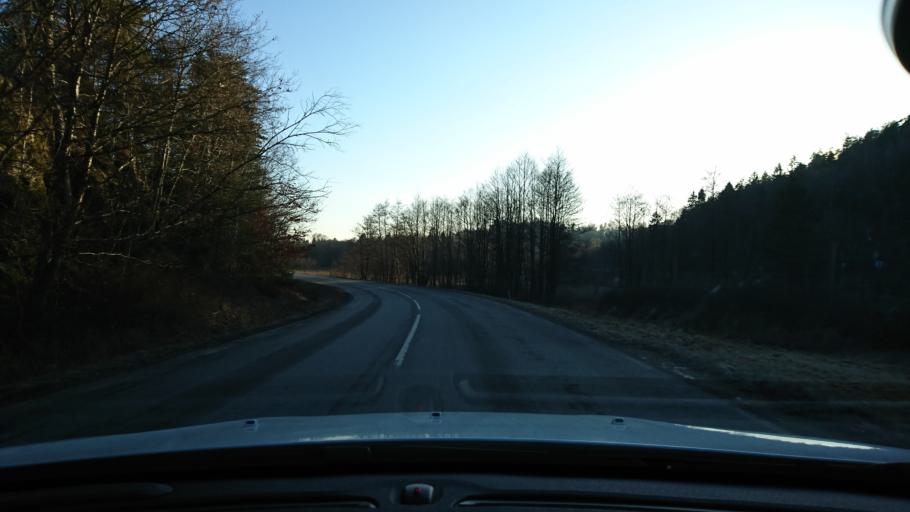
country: SE
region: Vaestra Goetaland
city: Svanesund
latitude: 58.1430
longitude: 11.8648
